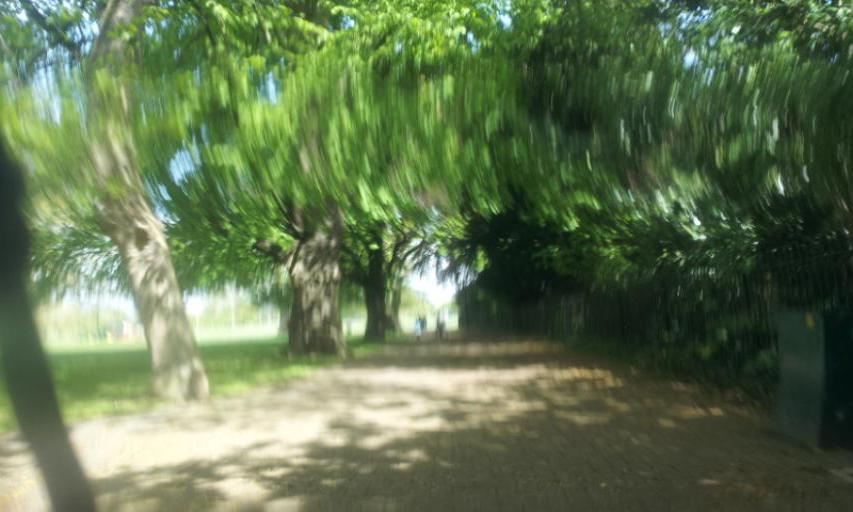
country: GB
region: England
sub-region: Greater London
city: Camberwell
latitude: 51.4575
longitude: -0.0643
